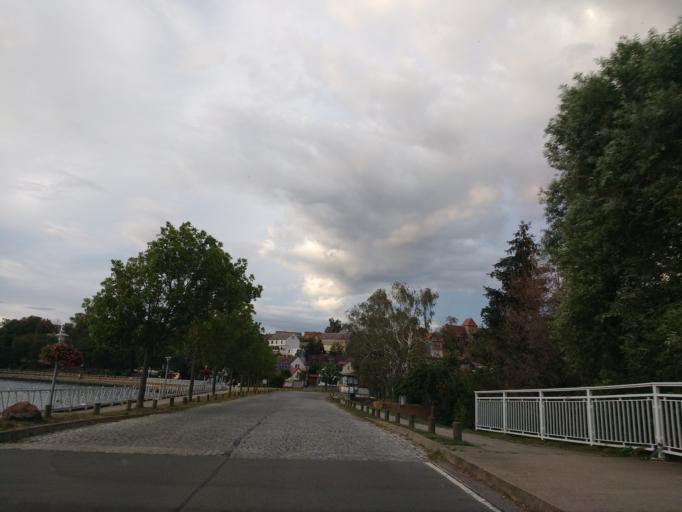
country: DE
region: Saxony-Anhalt
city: Roblingen am See
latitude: 51.4873
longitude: 11.7013
